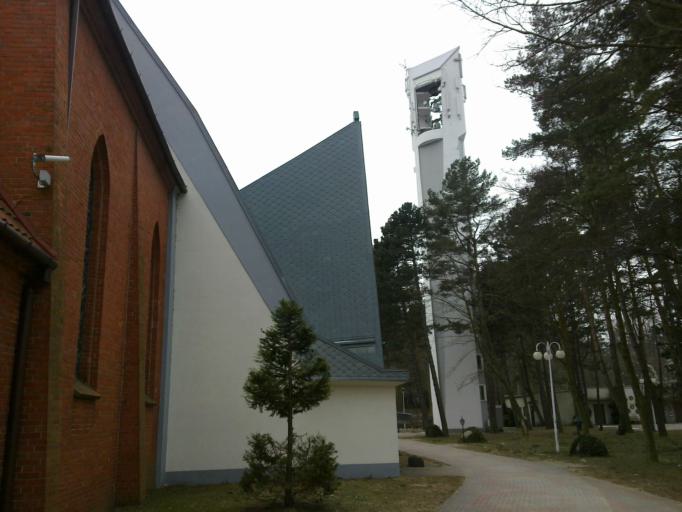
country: PL
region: Pomeranian Voivodeship
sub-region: Powiat pucki
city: Wladyslawowo
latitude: 54.7978
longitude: 18.3969
